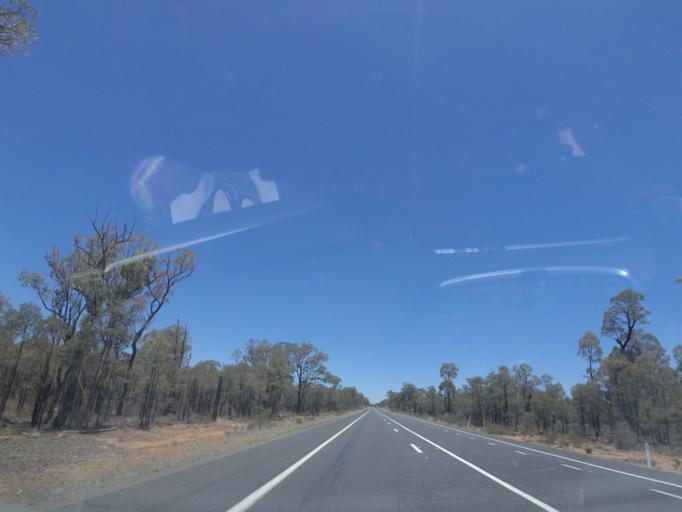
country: AU
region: New South Wales
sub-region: Warrumbungle Shire
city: Coonabarabran
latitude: -30.8673
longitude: 149.4516
